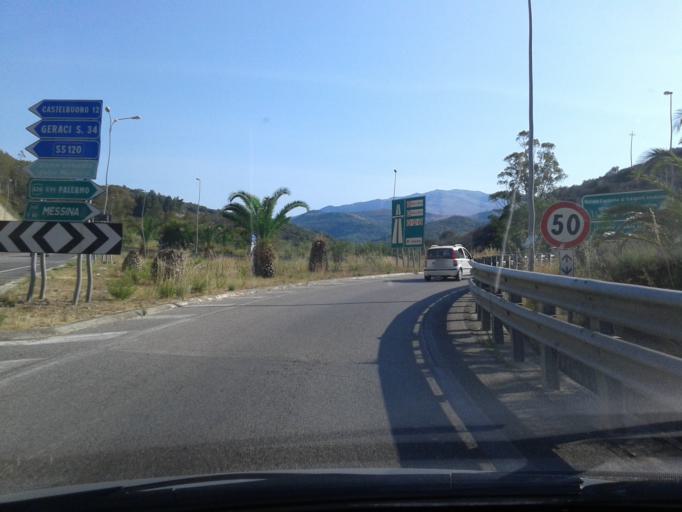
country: IT
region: Sicily
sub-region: Palermo
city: Pollina
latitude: 38.0065
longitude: 14.0995
